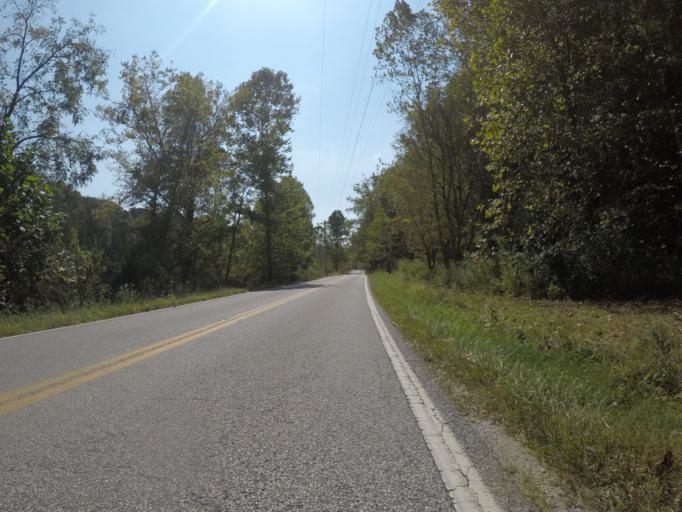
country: US
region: West Virginia
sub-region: Cabell County
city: Lesage
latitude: 38.5607
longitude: -82.3935
